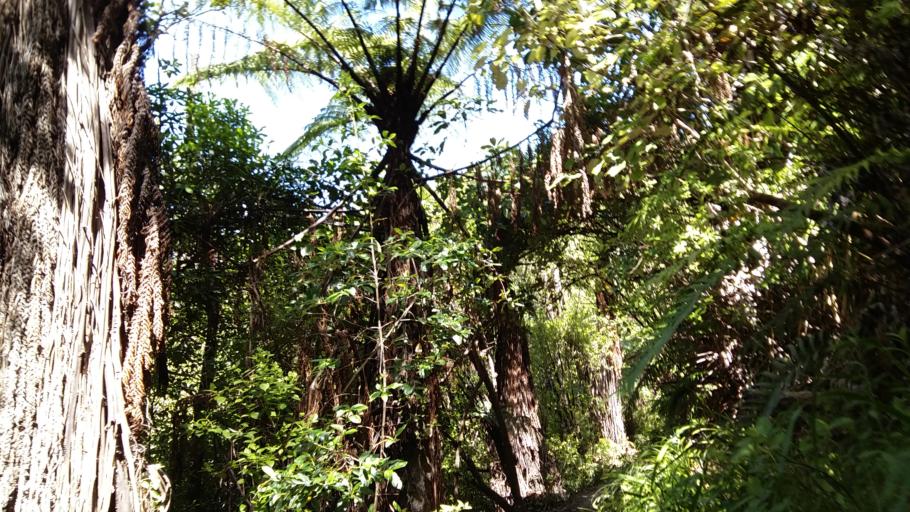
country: NZ
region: Bay of Plenty
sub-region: Whakatane District
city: Whakatane
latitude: -37.9417
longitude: 177.0156
